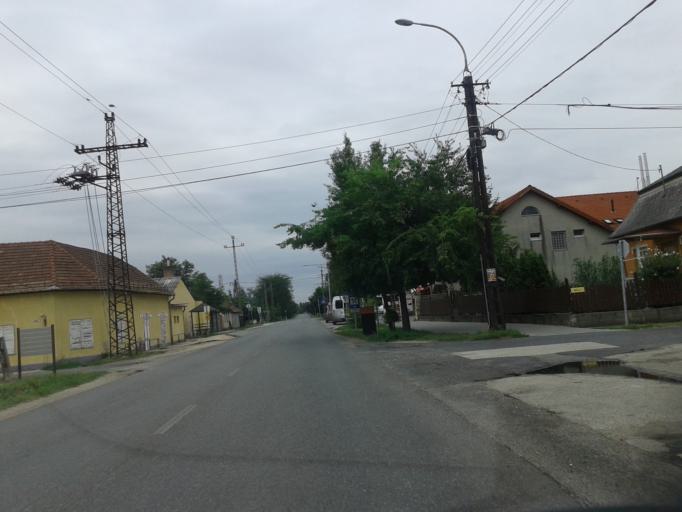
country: HU
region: Pest
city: Halasztelek
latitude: 47.3584
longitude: 18.9859
